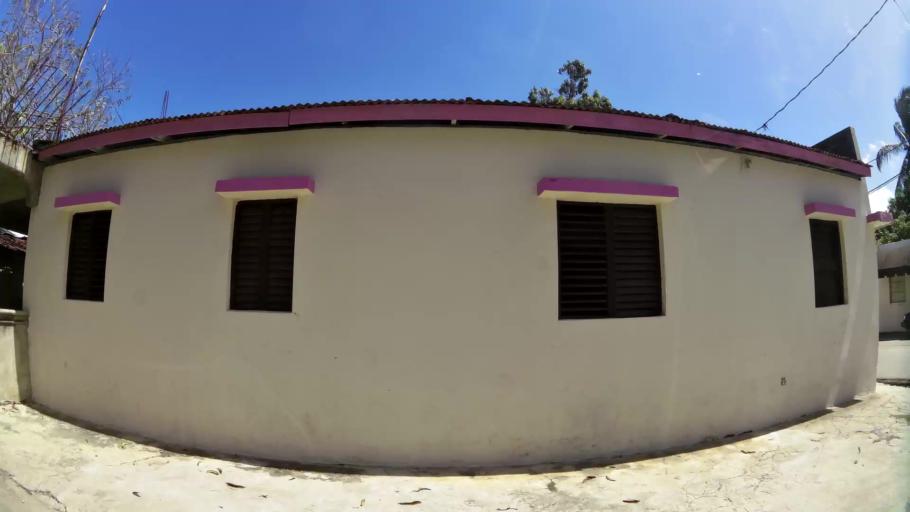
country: DO
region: San Cristobal
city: San Cristobal
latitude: 18.4005
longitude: -70.1072
